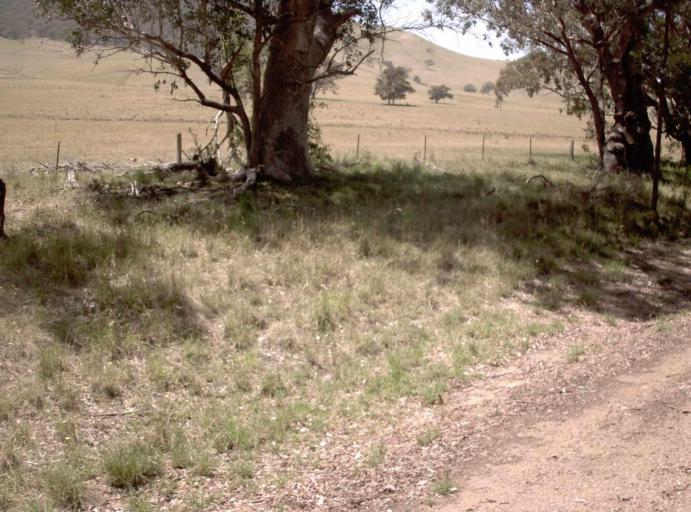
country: AU
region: Victoria
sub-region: East Gippsland
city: Bairnsdale
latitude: -37.3337
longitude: 147.7838
